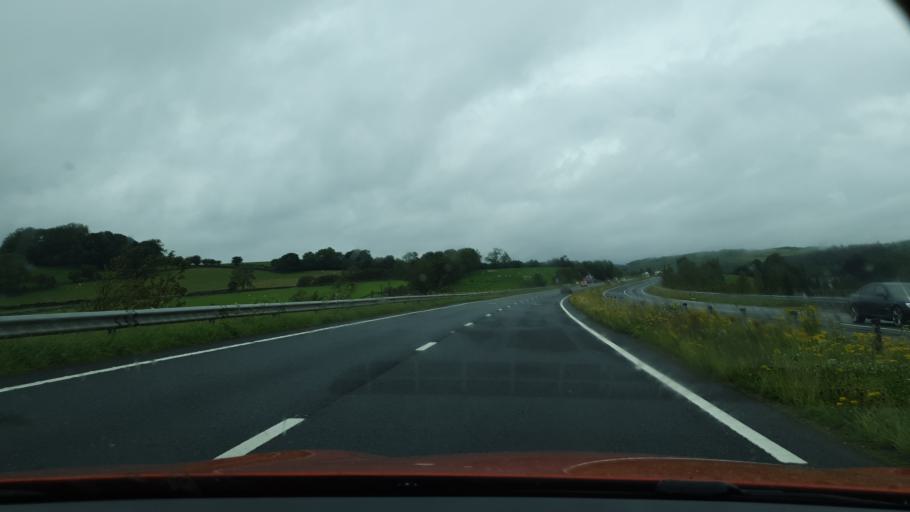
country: GB
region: England
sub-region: Cumbria
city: Grange-over-Sands
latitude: 54.2278
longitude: -2.9128
